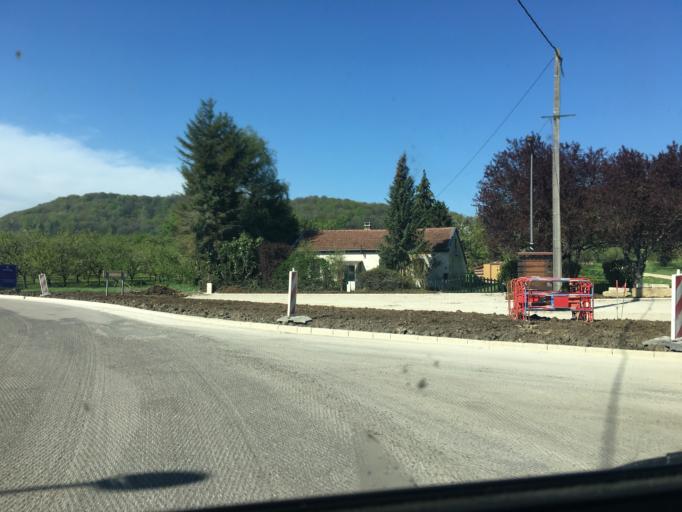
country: FR
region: Lorraine
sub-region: Departement de la Meuse
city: Vigneulles-les-Hattonchatel
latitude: 48.9315
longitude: 5.6916
